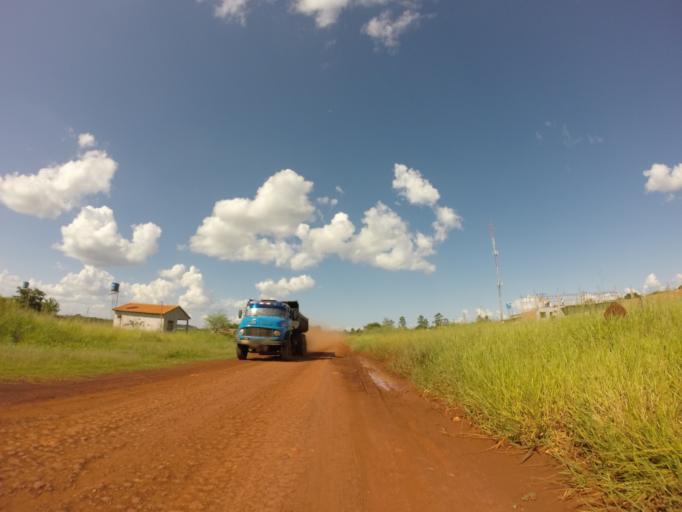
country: PY
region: Alto Parana
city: Ciudad del Este
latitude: -25.3729
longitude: -54.6547
